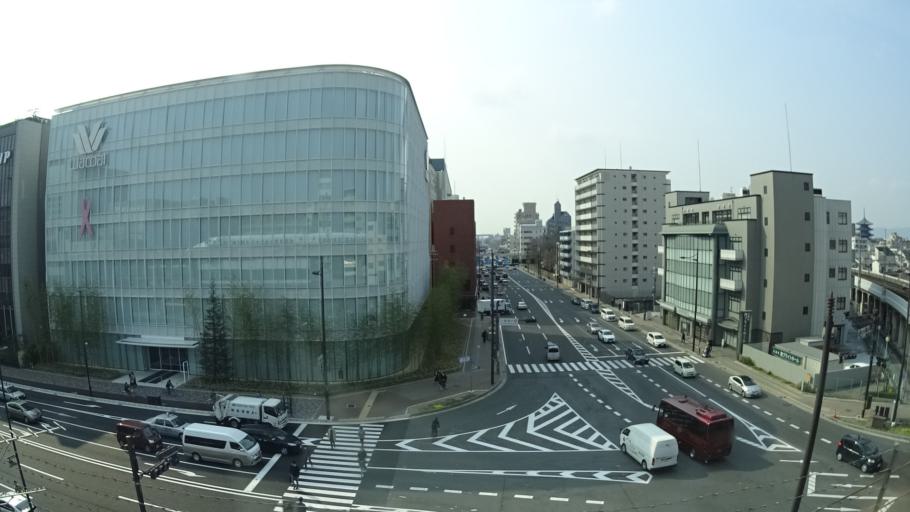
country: JP
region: Kyoto
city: Kyoto
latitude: 34.9845
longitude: 135.7540
